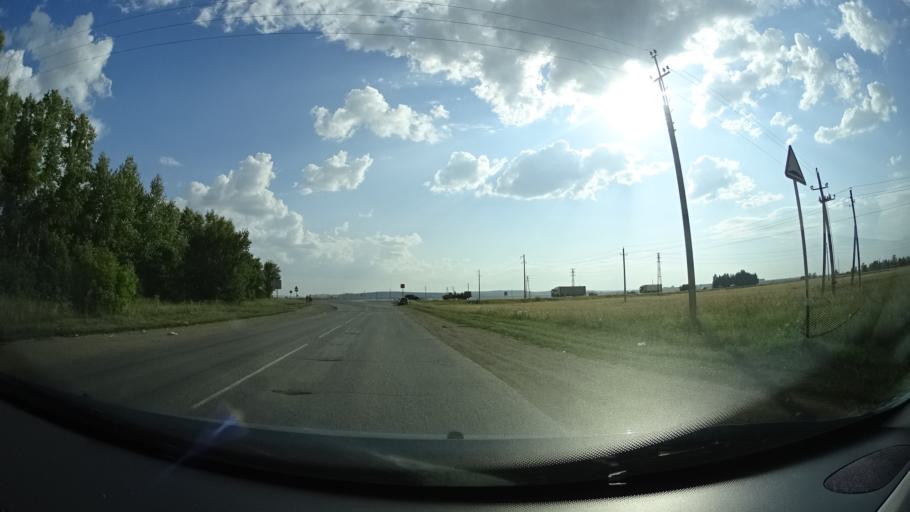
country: RU
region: Bashkortostan
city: Oktyabr'skiy
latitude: 54.4788
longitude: 53.3995
